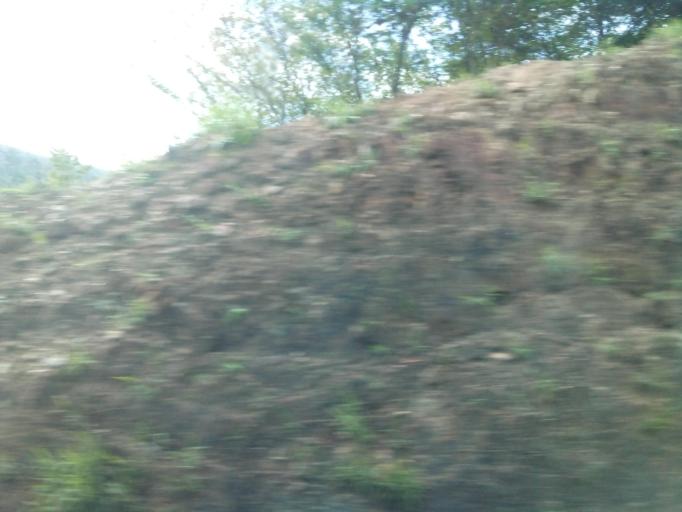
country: BR
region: Minas Gerais
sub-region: Santa Luzia
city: Santa Luzia
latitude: -19.8697
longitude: -43.8417
